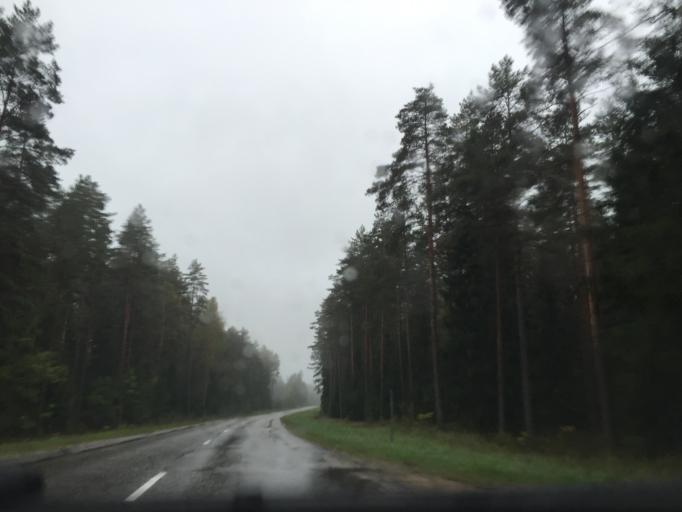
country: LV
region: Ropazu
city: Ropazi
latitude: 57.0213
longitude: 24.6836
